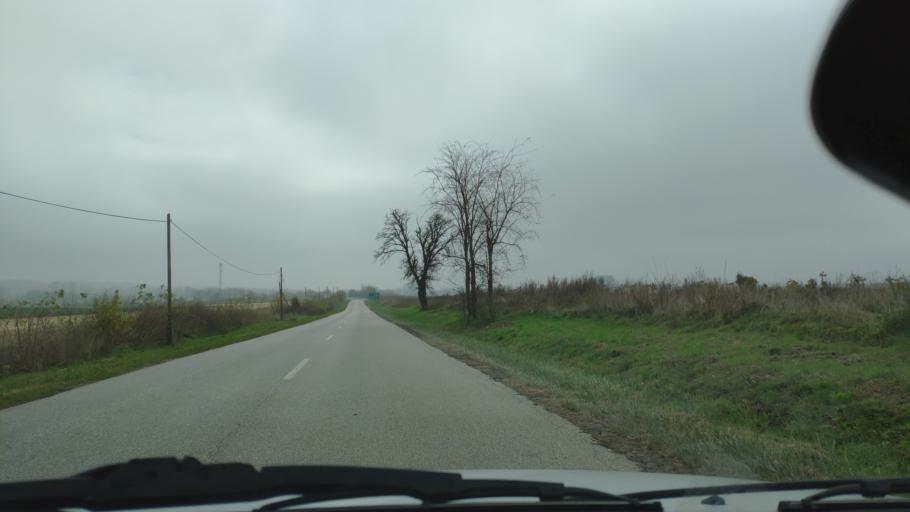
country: HU
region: Somogy
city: Balatonbereny
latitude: 46.6558
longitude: 17.2965
